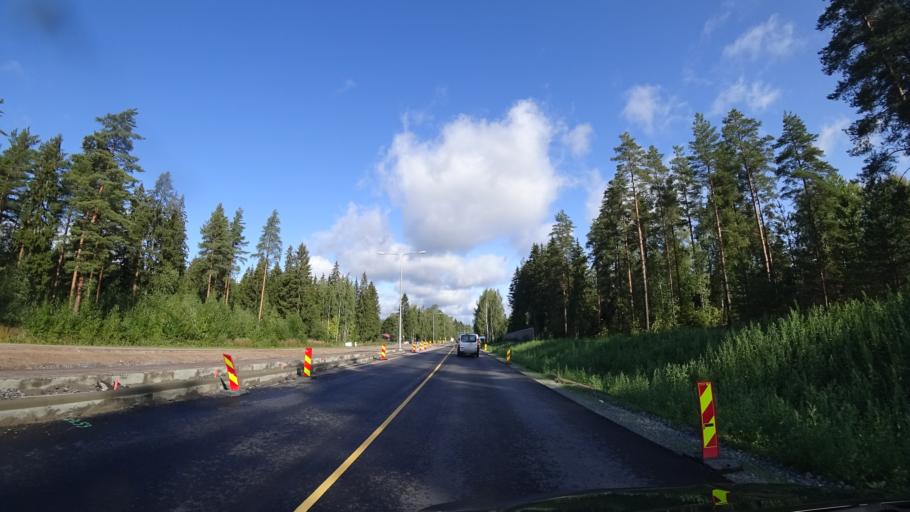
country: FI
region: Uusimaa
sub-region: Helsinki
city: Tuusula
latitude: 60.4125
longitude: 25.0034
